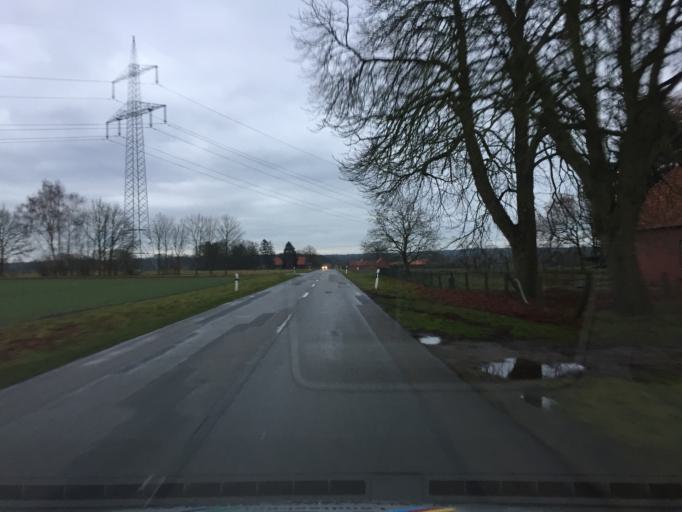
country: DE
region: Lower Saxony
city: Pennigsehl
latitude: 52.6387
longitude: 9.0050
